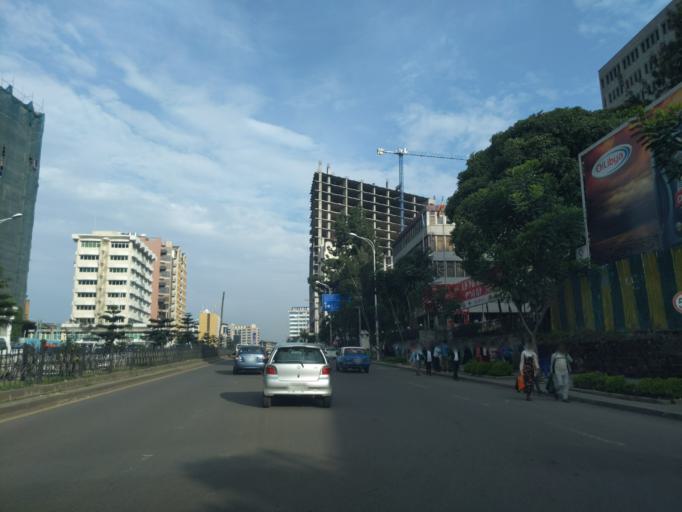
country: ET
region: Adis Abeba
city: Addis Ababa
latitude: 9.0099
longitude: 38.7636
